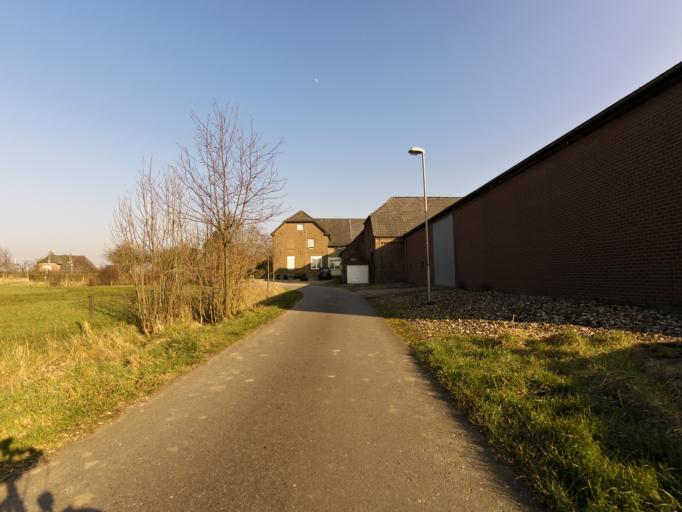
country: DE
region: North Rhine-Westphalia
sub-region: Regierungsbezirk Dusseldorf
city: Emmerich
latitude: 51.8443
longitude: 6.2874
